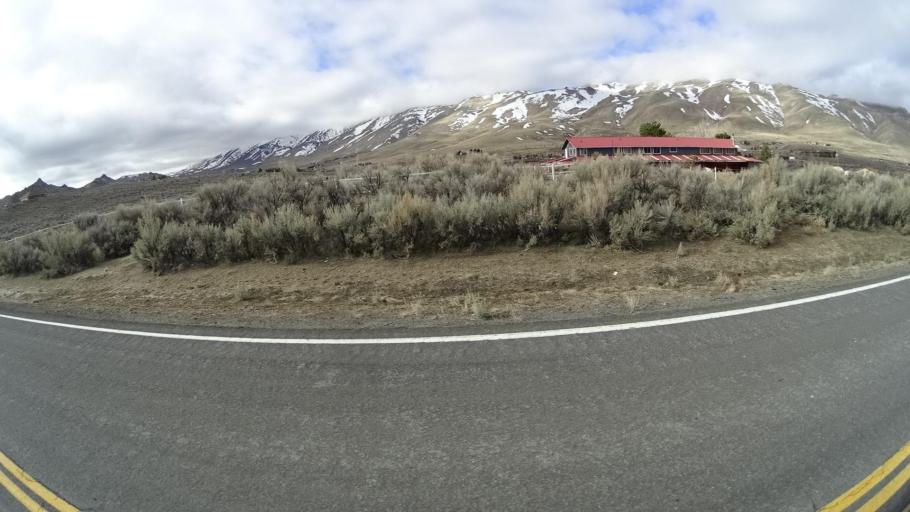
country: US
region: Nevada
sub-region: Washoe County
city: Cold Springs
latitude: 39.8683
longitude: -119.9513
